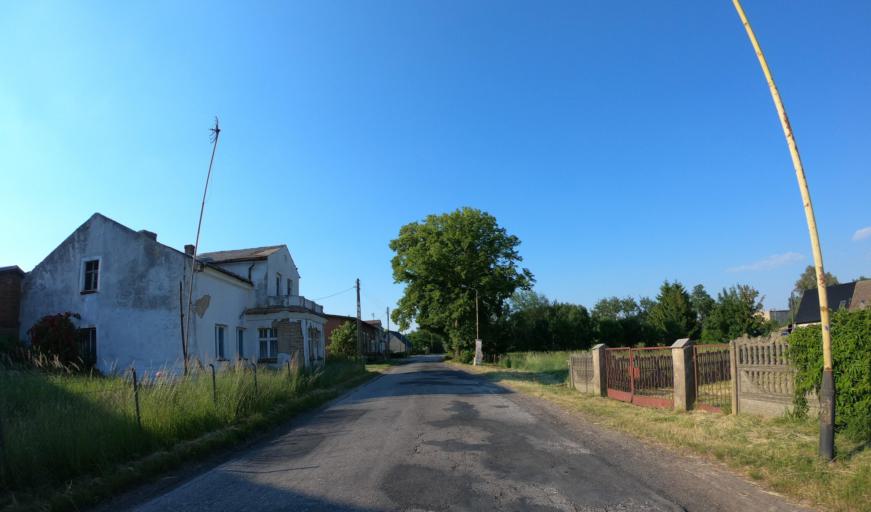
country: PL
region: West Pomeranian Voivodeship
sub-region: Powiat lobeski
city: Dobra
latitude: 53.5324
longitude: 15.3138
